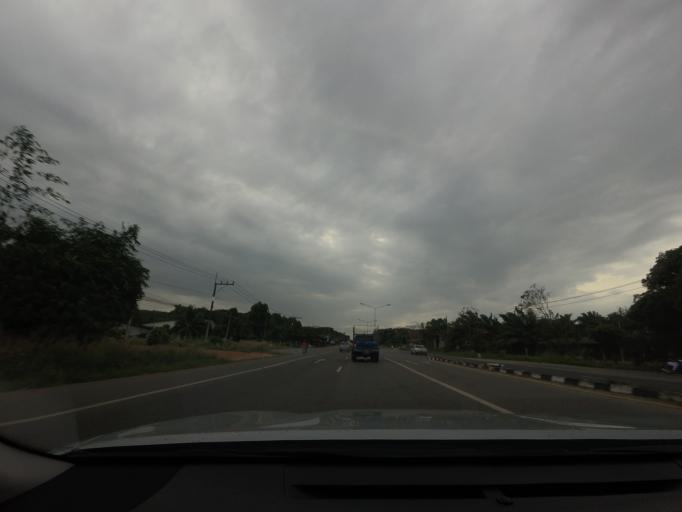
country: TH
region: Surat Thani
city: Phunphin
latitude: 9.0466
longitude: 99.1573
